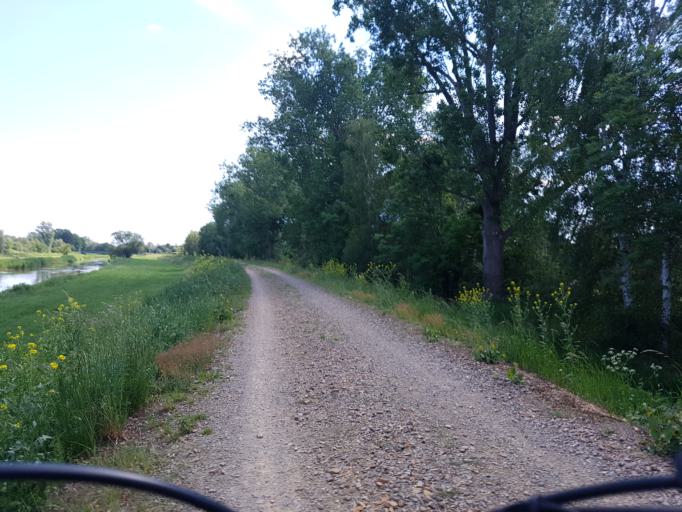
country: DE
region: Brandenburg
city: Bad Liebenwerda
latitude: 51.5254
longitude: 13.3842
